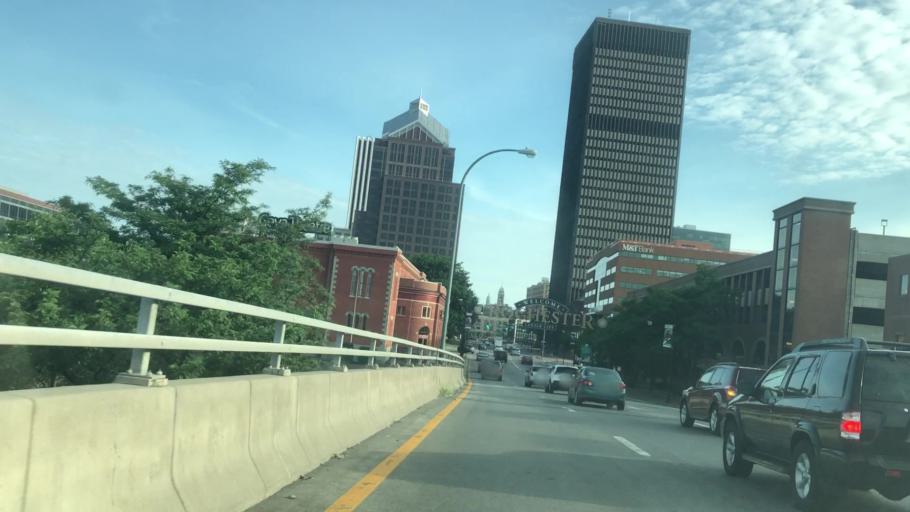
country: US
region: New York
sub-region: Monroe County
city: Rochester
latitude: 43.1514
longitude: -77.6045
